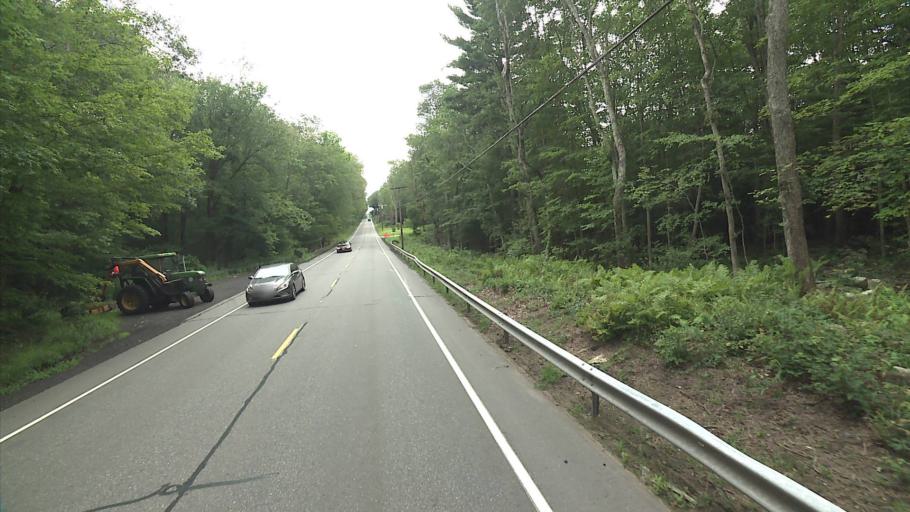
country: US
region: Connecticut
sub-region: Tolland County
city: Storrs
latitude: 41.8673
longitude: -72.2009
